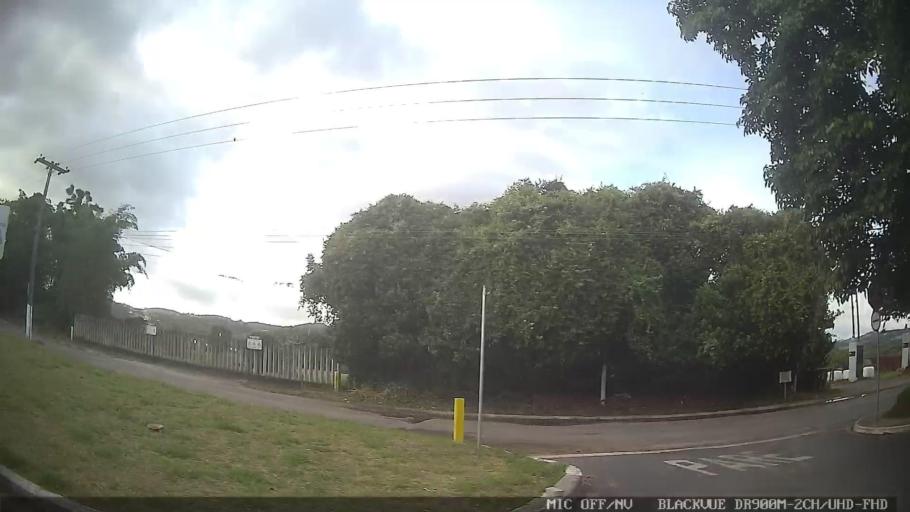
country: BR
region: Sao Paulo
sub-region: Atibaia
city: Atibaia
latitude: -23.1063
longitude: -46.5285
